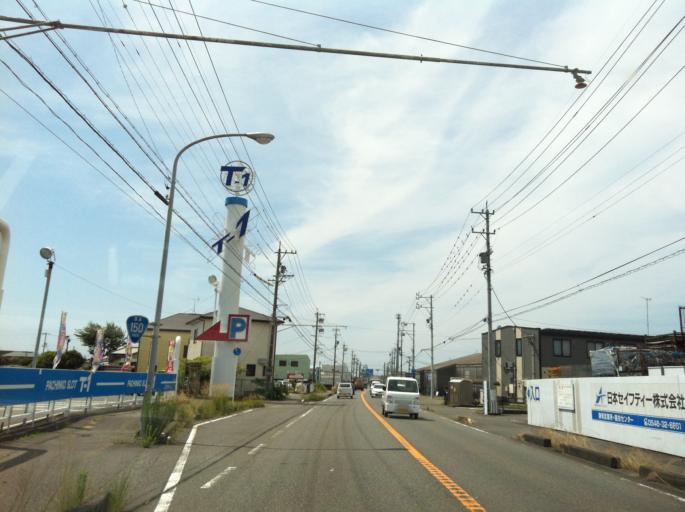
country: JP
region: Shizuoka
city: Shimada
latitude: 34.7833
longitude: 138.2547
